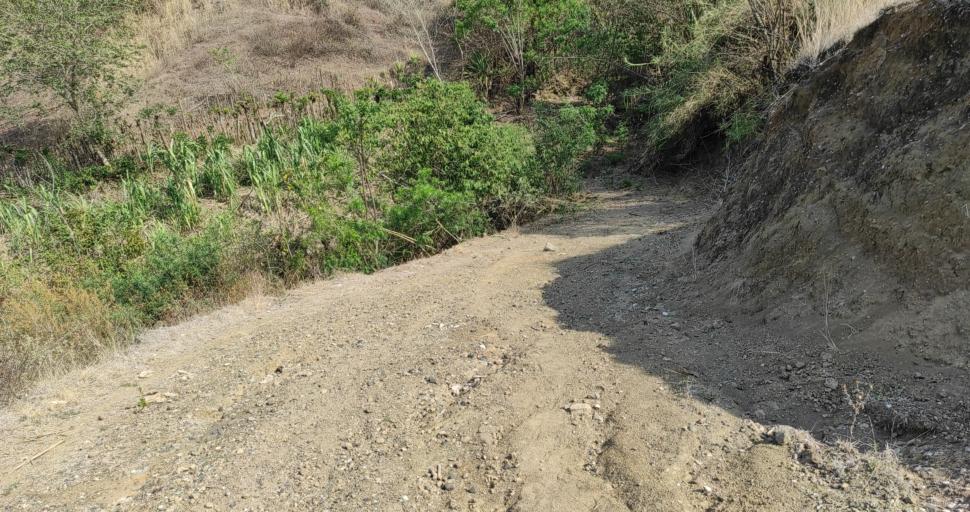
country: EC
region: Loja
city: Catacocha
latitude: -3.9996
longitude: -79.7151
